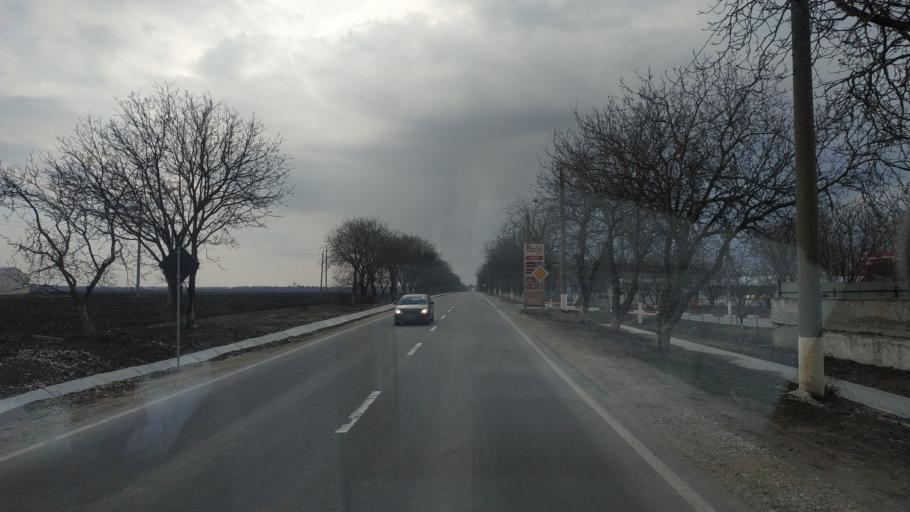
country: MD
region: Telenesti
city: Grigoriopol
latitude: 47.0160
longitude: 29.2894
